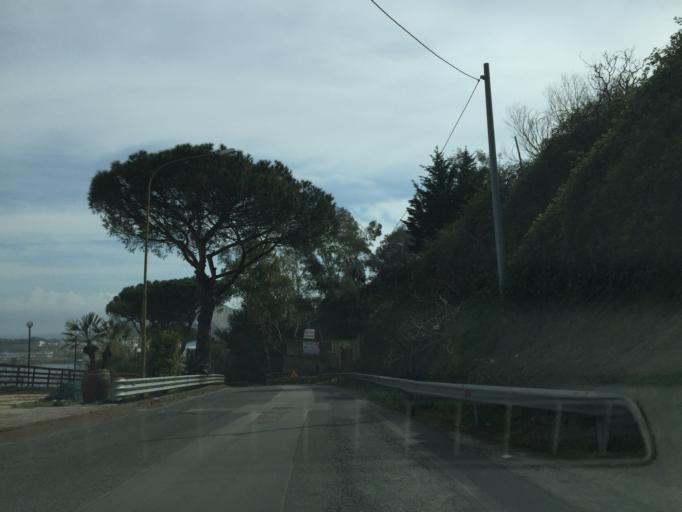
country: IT
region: Campania
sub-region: Provincia di Napoli
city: Monte di Procida
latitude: 40.7938
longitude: 14.0632
